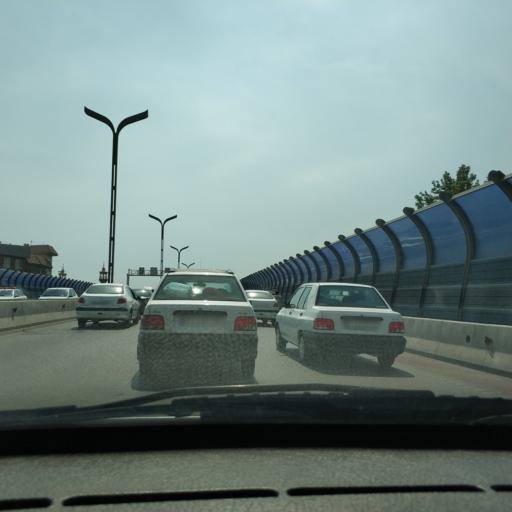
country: IR
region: Tehran
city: Tajrish
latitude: 35.7859
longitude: 51.4440
